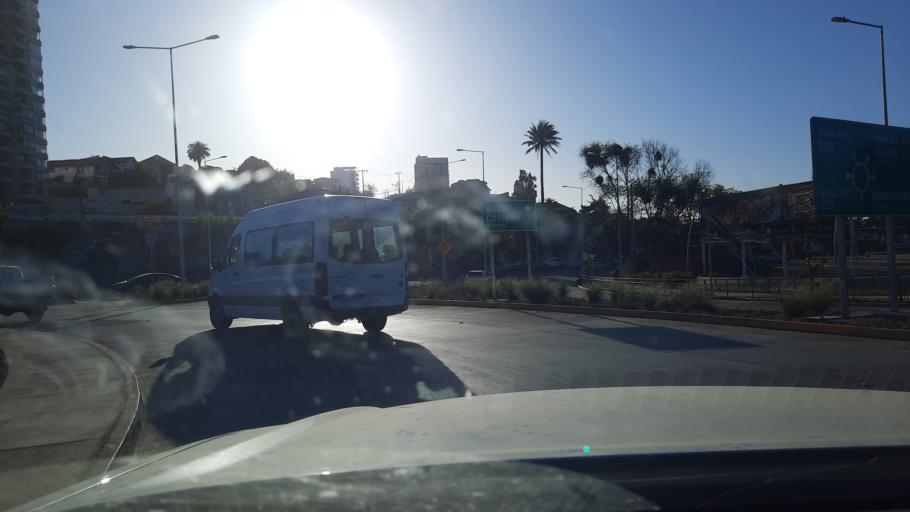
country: CL
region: Valparaiso
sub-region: Provincia de Valparaiso
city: Vina del Mar
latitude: -32.9213
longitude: -71.5069
